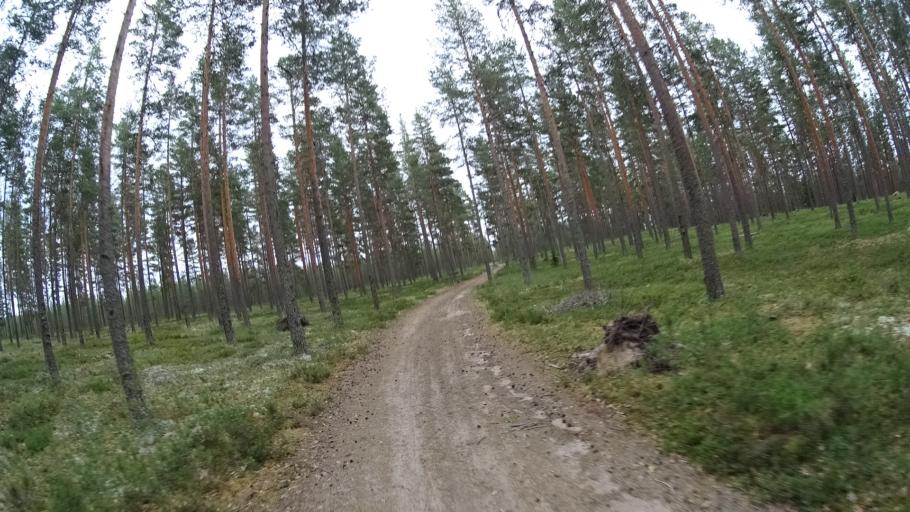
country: FI
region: Satakunta
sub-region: Pohjois-Satakunta
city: Jaemijaervi
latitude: 61.7636
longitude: 22.7696
